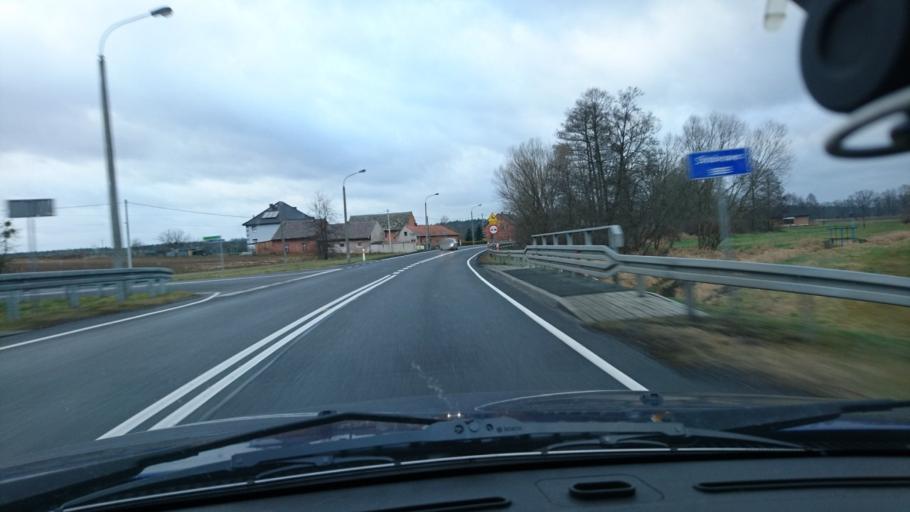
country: PL
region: Opole Voivodeship
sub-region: Powiat oleski
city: Olesno
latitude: 50.9126
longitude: 18.3504
